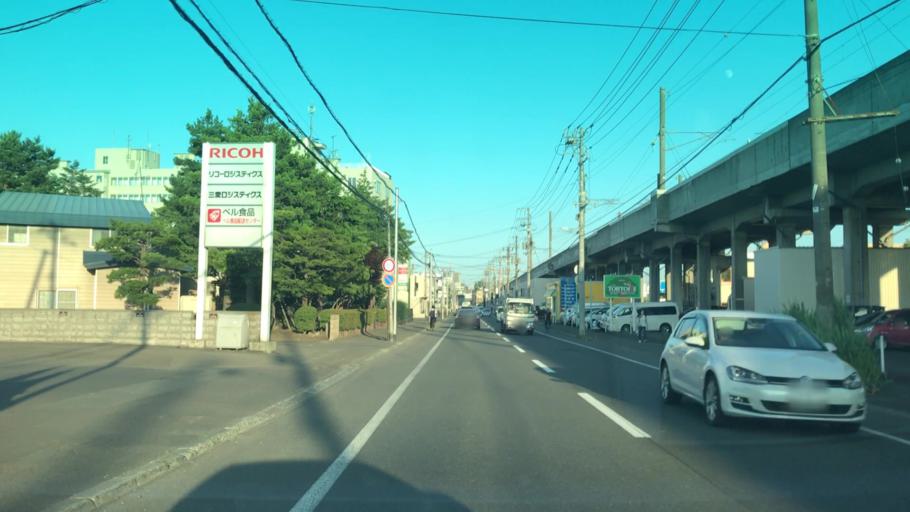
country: JP
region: Hokkaido
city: Sapporo
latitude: 43.0785
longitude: 141.3142
